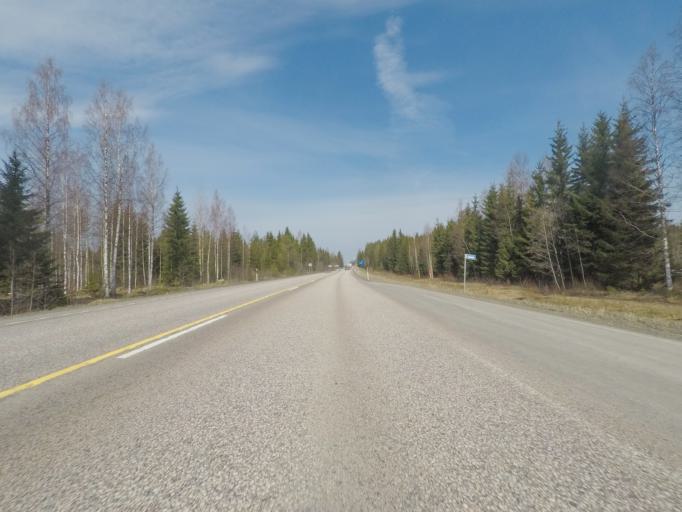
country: FI
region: Central Finland
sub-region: Joutsa
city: Joutsa
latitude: 61.7823
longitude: 26.0954
